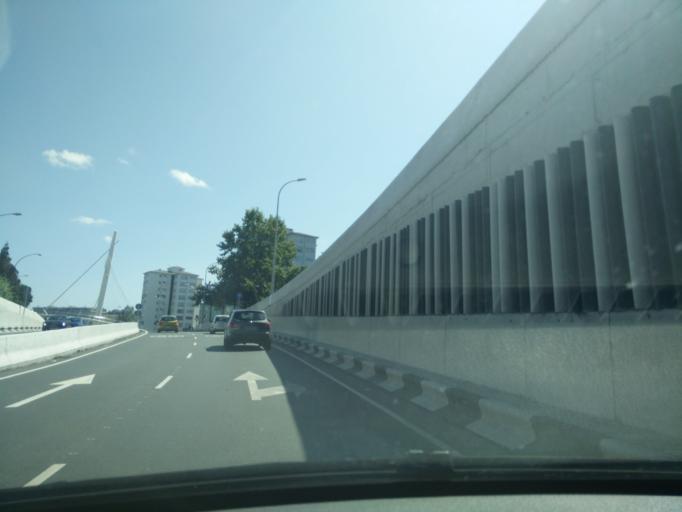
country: ES
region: Galicia
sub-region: Provincia da Coruna
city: A Coruna
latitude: 43.3433
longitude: -8.4133
